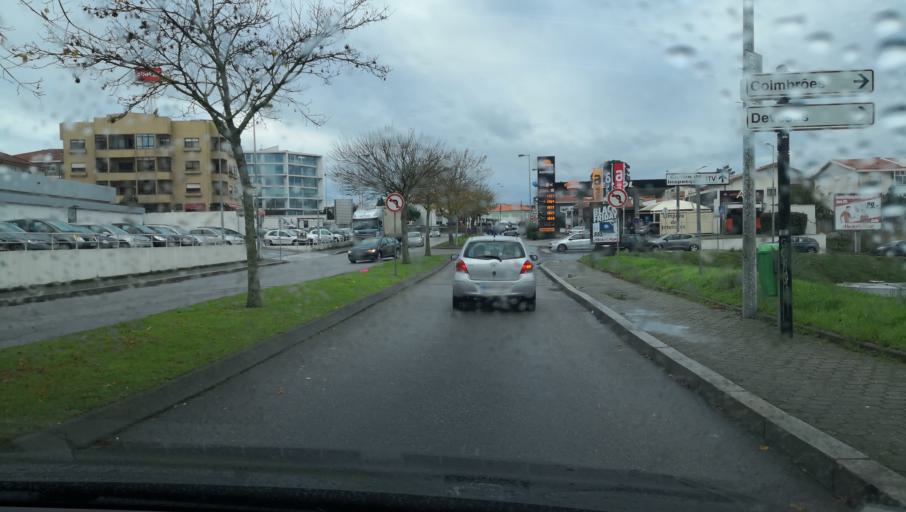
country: PT
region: Porto
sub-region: Vila Nova de Gaia
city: Vila Nova de Gaia
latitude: 41.1200
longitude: -8.6259
